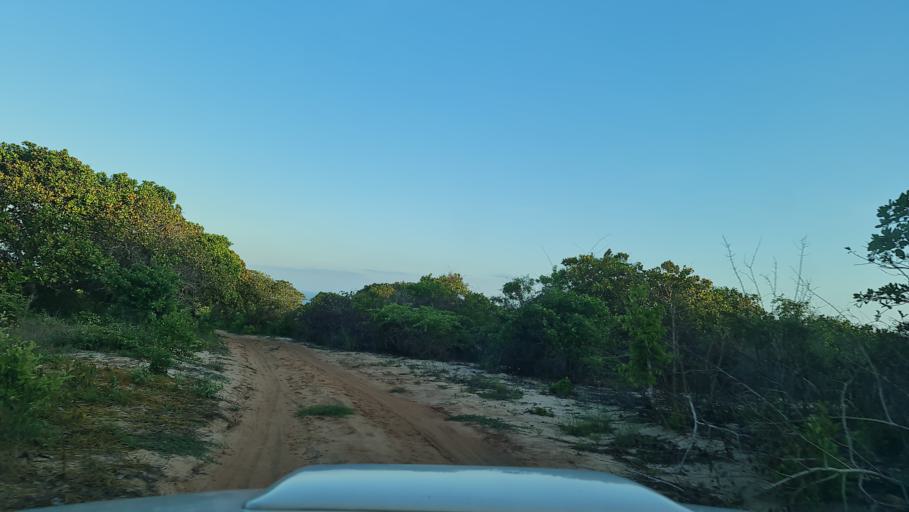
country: MZ
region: Nampula
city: Ilha de Mocambique
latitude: -15.6346
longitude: 40.4128
